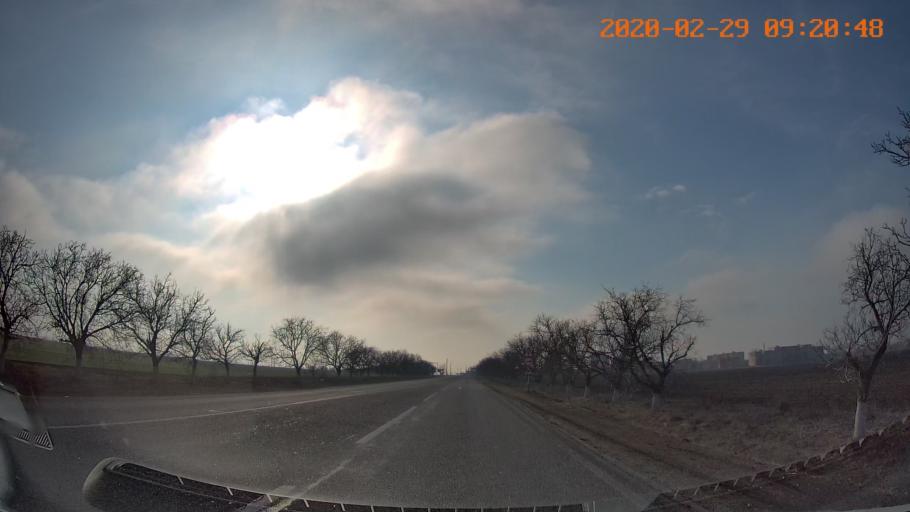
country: MD
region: Telenesti
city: Pervomaisc
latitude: 46.7434
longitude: 29.9528
